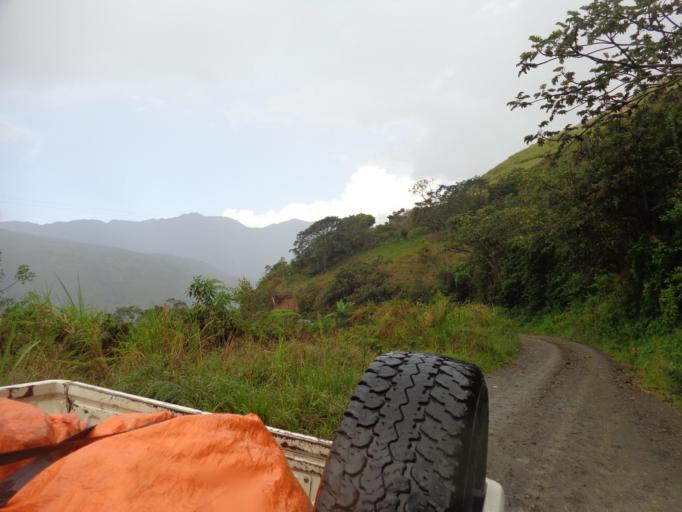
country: BO
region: La Paz
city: Coroico
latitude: -16.1410
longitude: -67.7461
